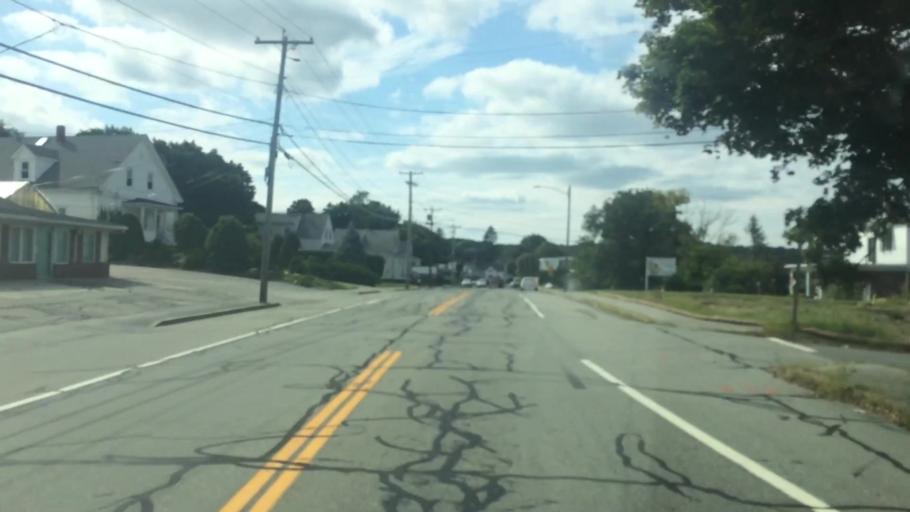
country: US
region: Rhode Island
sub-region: Providence County
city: Cranston
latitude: 41.7933
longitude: -71.4759
